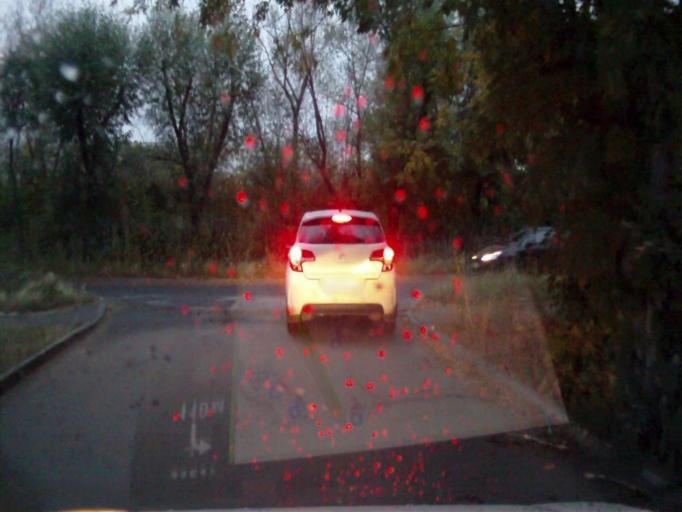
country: RU
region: Chelyabinsk
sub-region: Gorod Chelyabinsk
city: Chelyabinsk
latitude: 55.1910
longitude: 61.3362
